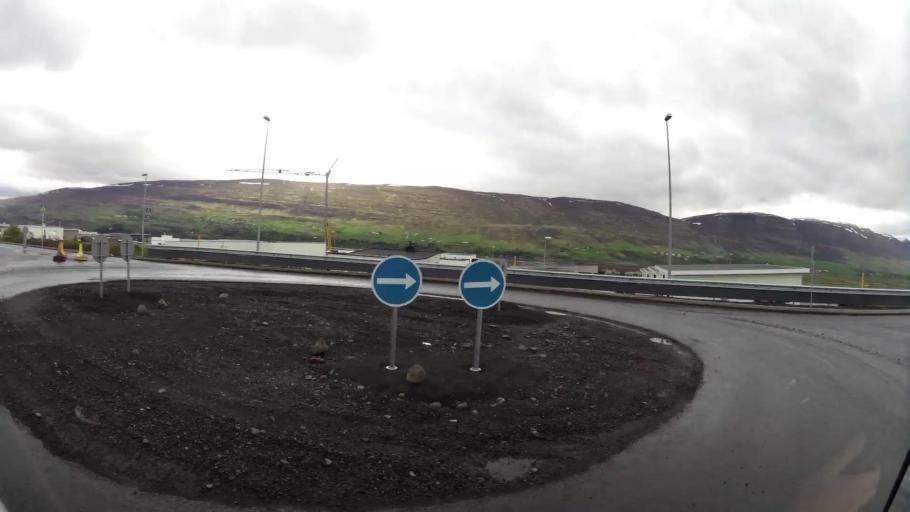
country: IS
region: Northeast
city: Akureyri
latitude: 65.6615
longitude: -18.0895
